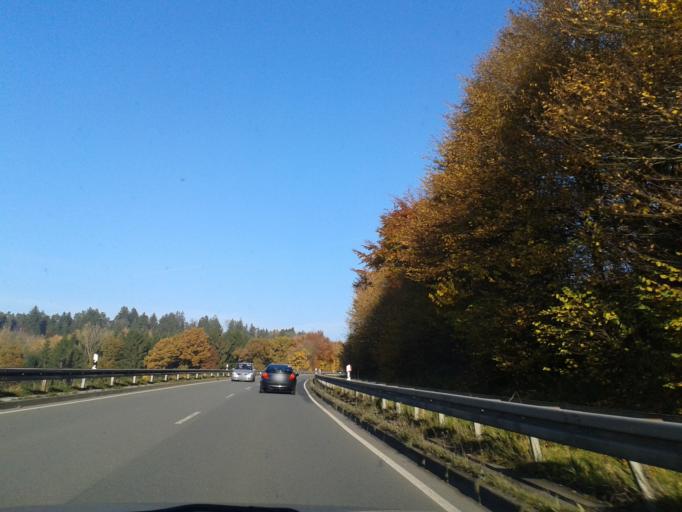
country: DE
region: North Rhine-Westphalia
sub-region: Regierungsbezirk Arnsberg
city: Ruthen
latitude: 51.4660
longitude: 8.4373
